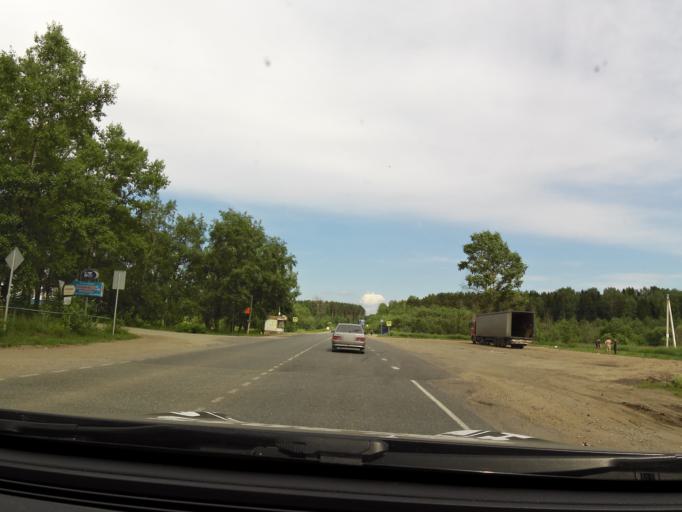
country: RU
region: Kirov
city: Vakhrushi
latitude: 58.6502
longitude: 49.8753
